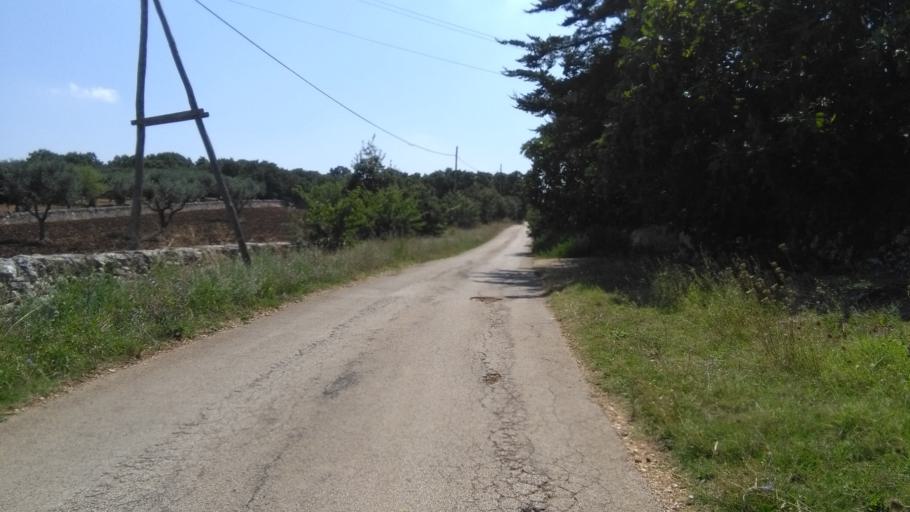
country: IT
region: Apulia
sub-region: Provincia di Bari
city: Noci
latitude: 40.8191
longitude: 17.1762
